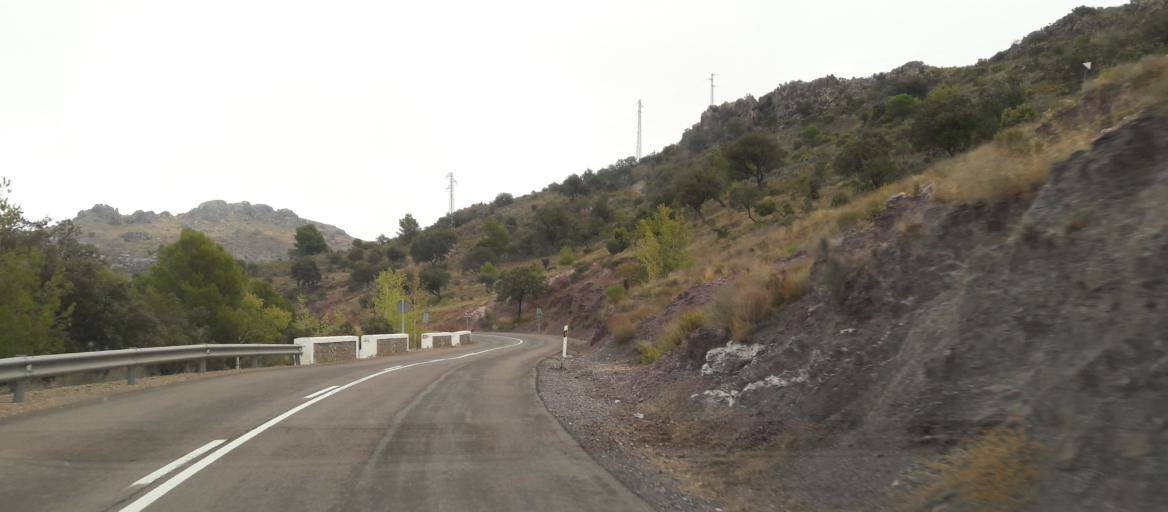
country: ES
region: Andalusia
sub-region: Provincia de Almeria
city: Enix
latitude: 36.8928
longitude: -2.6152
